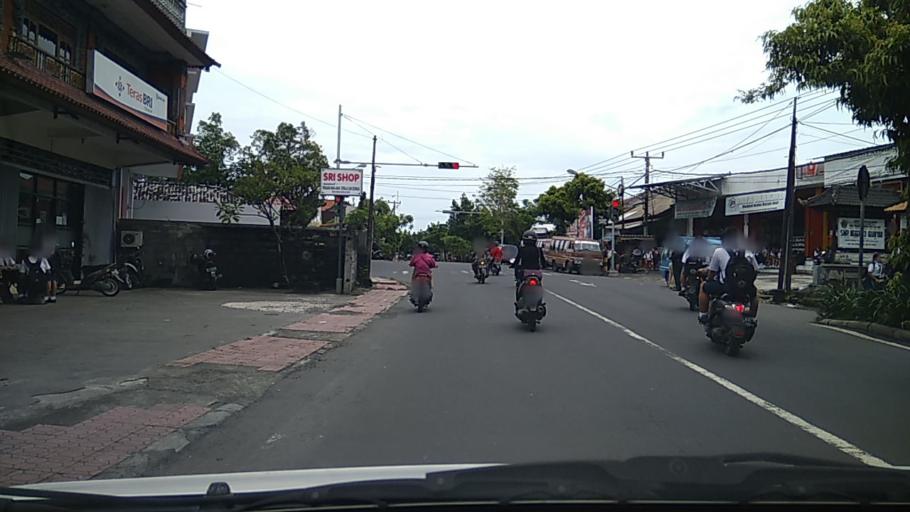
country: ID
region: Bali
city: Banjar Kelodan
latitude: -8.5409
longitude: 115.3470
